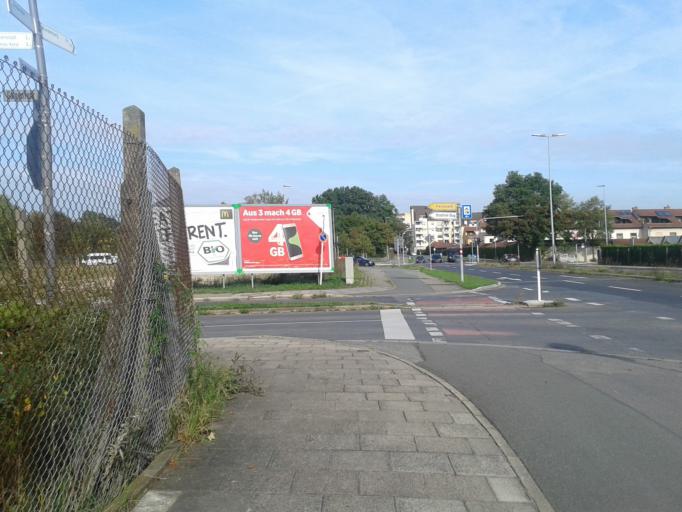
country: DE
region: Bavaria
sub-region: Upper Franconia
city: Bamberg
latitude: 49.8828
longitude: 10.9132
